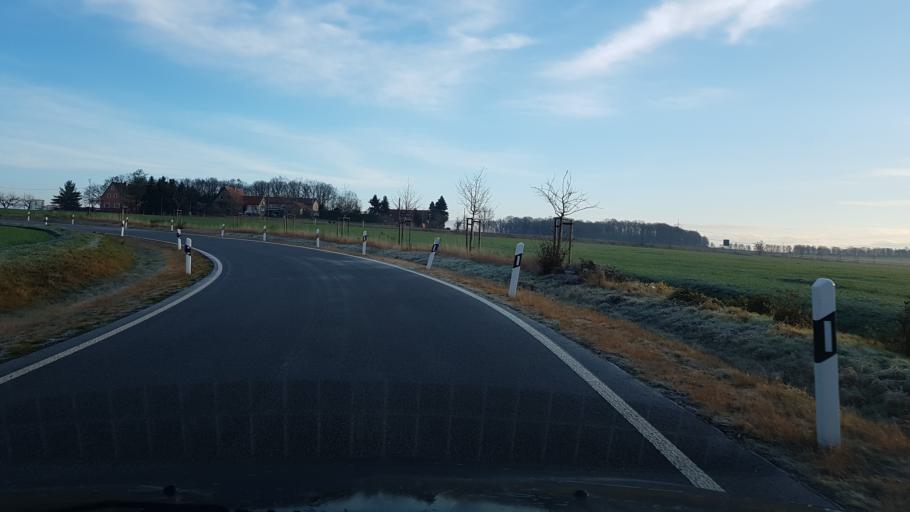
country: DE
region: Saxony
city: Neschwitz
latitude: 51.2468
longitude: 14.3542
